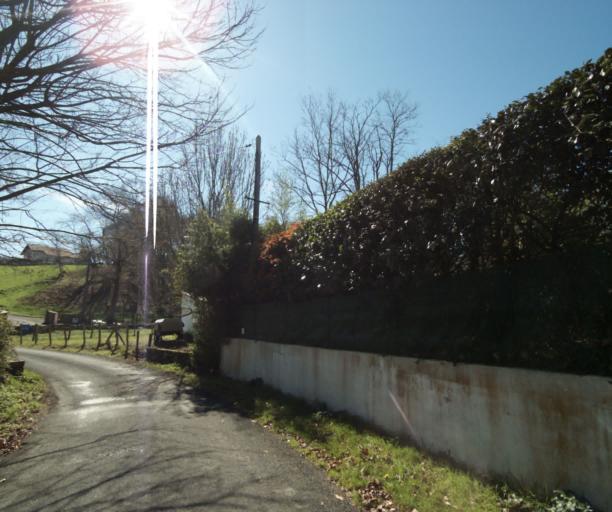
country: FR
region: Aquitaine
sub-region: Departement des Pyrenees-Atlantiques
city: Urrugne
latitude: 43.3392
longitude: -1.6946
